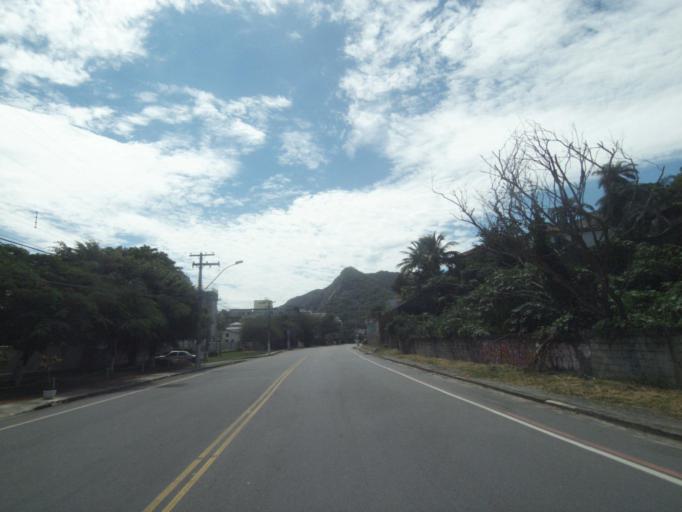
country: BR
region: Rio de Janeiro
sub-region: Niteroi
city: Niteroi
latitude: -22.9652
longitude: -43.0350
